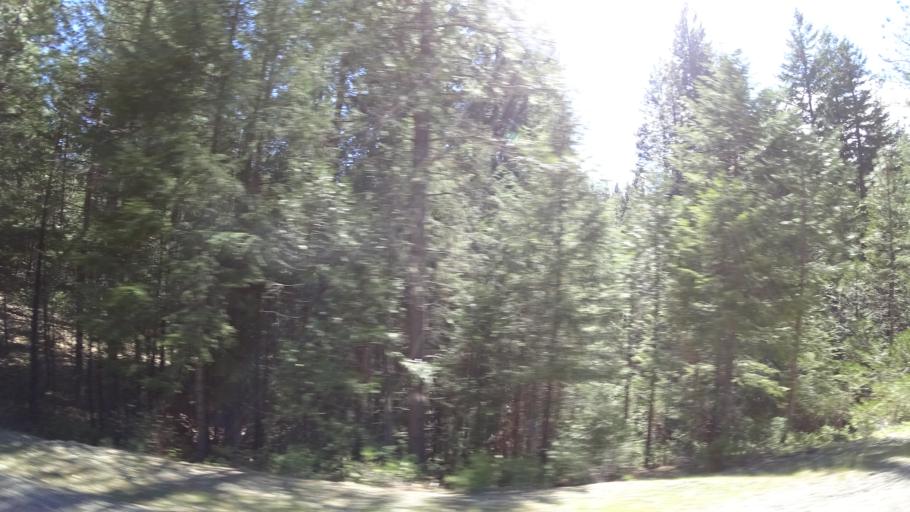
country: US
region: California
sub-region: Trinity County
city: Lewiston
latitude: 40.9060
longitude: -122.7848
